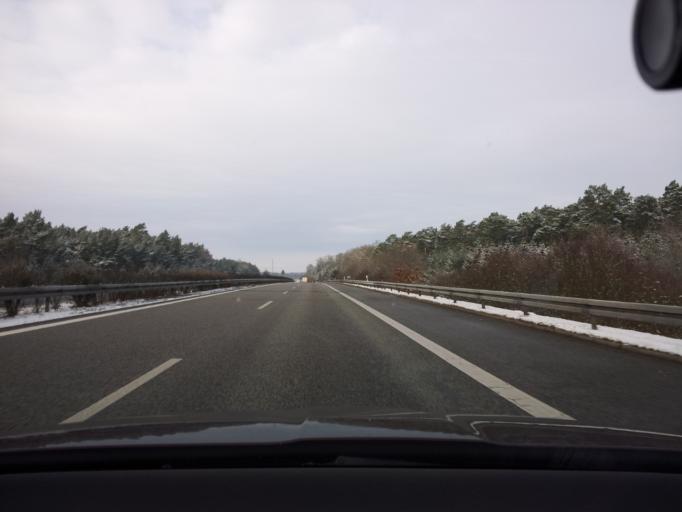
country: DE
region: Mecklenburg-Vorpommern
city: Sulstorf
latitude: 53.4783
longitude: 11.2955
